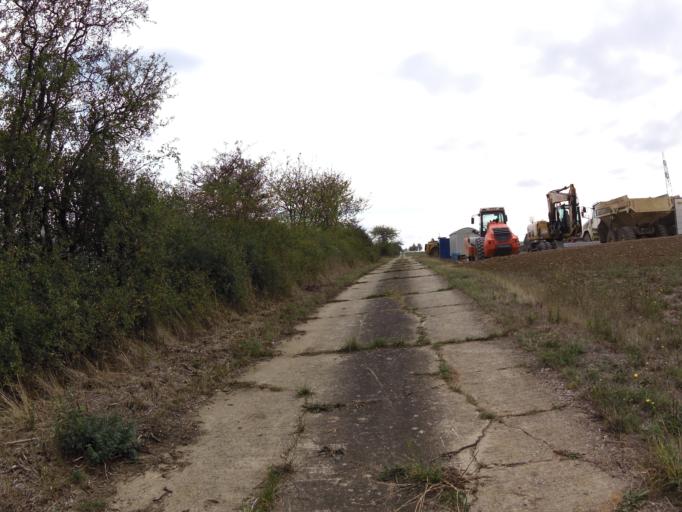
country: DE
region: Bavaria
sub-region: Regierungsbezirk Unterfranken
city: Waldbrunn
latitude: 49.7622
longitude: 9.8098
